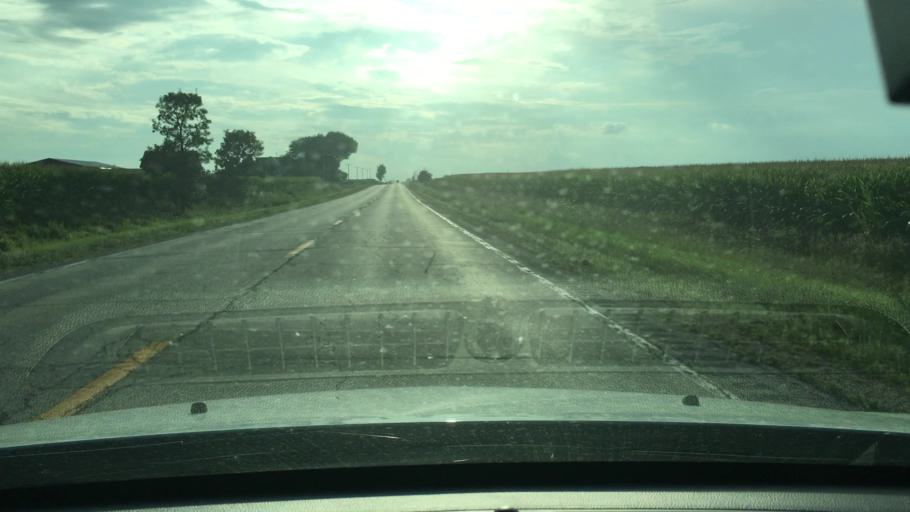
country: US
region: Illinois
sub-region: DeKalb County
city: Malta
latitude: 41.9355
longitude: -88.9193
